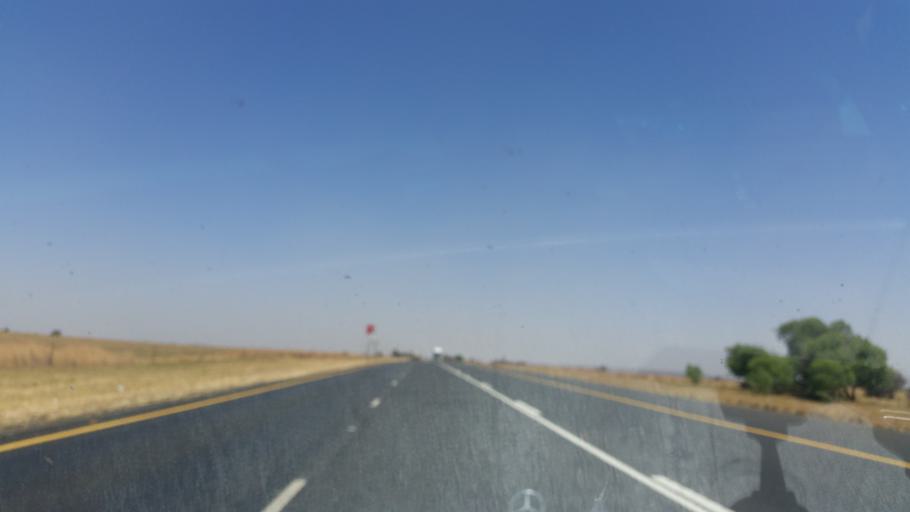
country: ZA
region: Orange Free State
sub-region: Lejweleputswa District Municipality
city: Winburg
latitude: -28.6450
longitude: 26.8838
